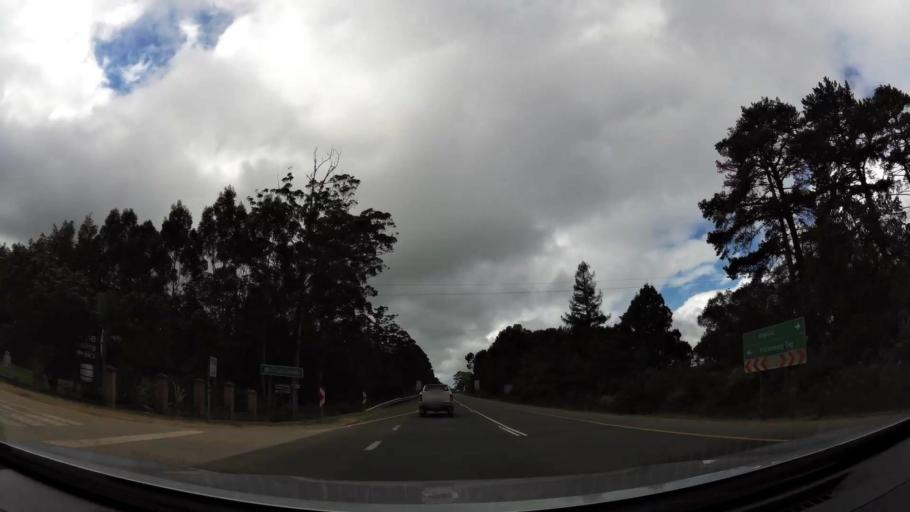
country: ZA
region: Western Cape
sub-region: Eden District Municipality
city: Plettenberg Bay
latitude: -34.0374
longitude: 23.2202
